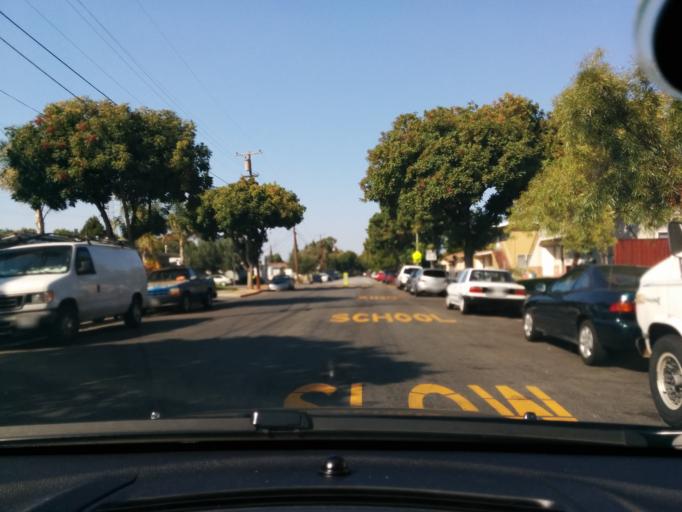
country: US
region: California
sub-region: Santa Clara County
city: Sunnyvale
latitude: 37.3908
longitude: -122.0109
